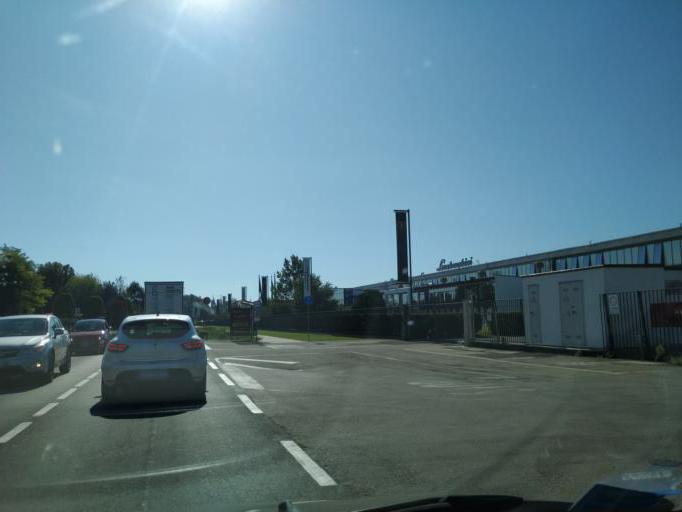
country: IT
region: Emilia-Romagna
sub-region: Provincia di Bologna
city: Sant'Agata Bolognese
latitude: 44.6602
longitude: 11.1242
